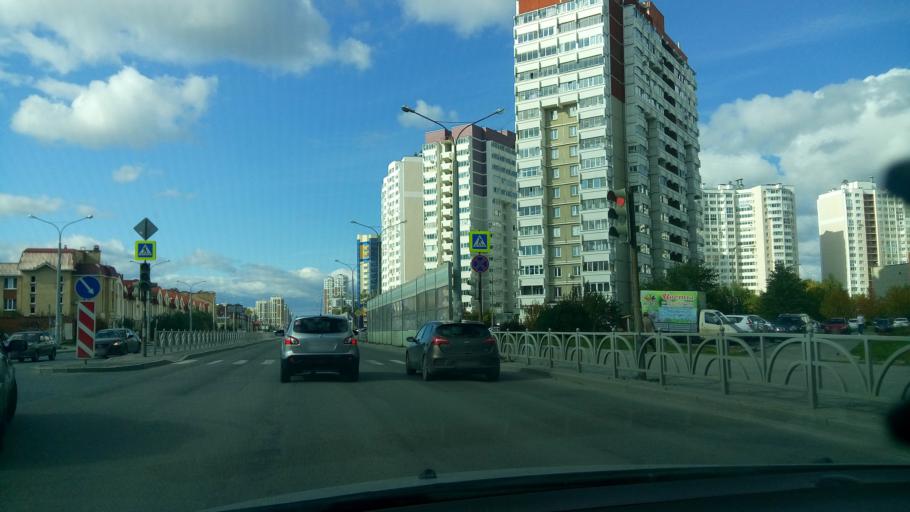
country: RU
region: Sverdlovsk
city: Sovkhoznyy
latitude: 56.7810
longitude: 60.5436
